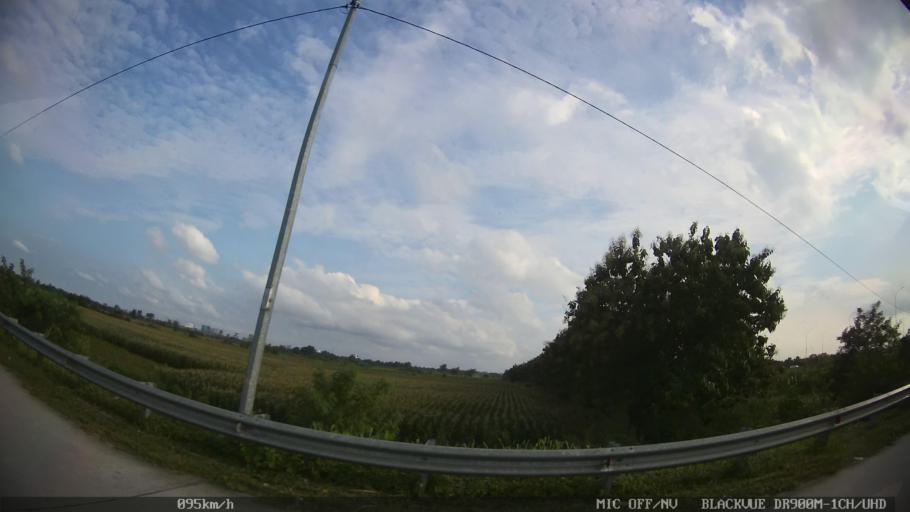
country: ID
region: North Sumatra
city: Medan
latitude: 3.6375
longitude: 98.6393
